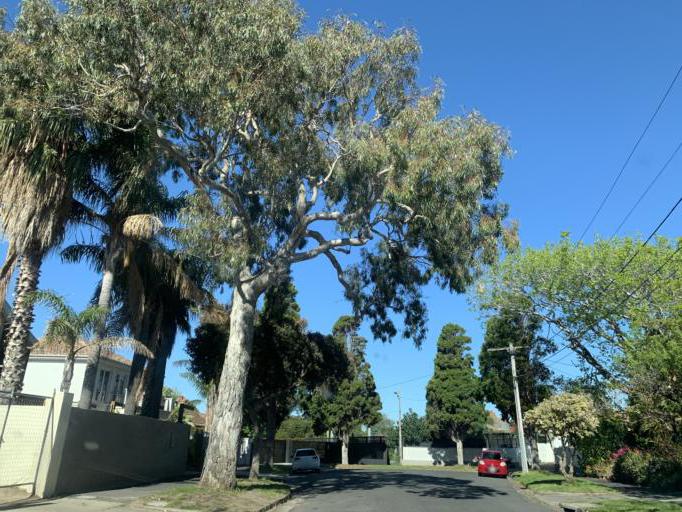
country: AU
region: Victoria
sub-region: Bayside
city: Hampton
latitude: -37.9226
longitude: 144.9904
